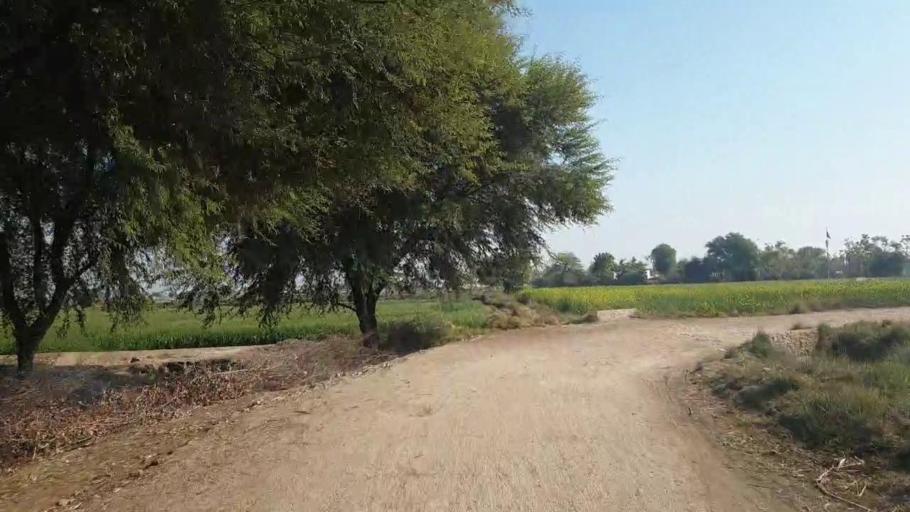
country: PK
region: Sindh
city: Shahpur Chakar
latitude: 26.0831
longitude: 68.5930
